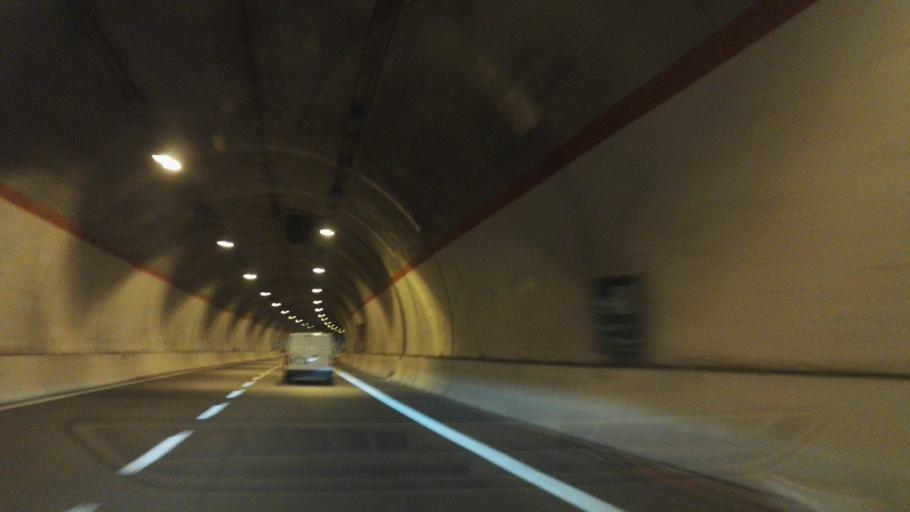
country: IT
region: Calabria
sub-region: Provincia di Catanzaro
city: Squillace Lido
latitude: 38.7867
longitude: 16.5504
